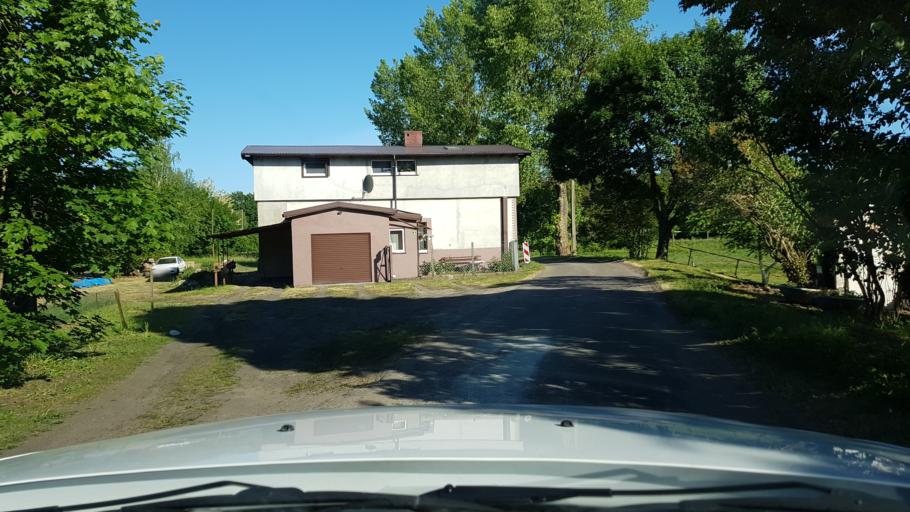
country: PL
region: West Pomeranian Voivodeship
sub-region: Powiat pyrzycki
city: Bielice
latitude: 53.2175
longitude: 14.6075
